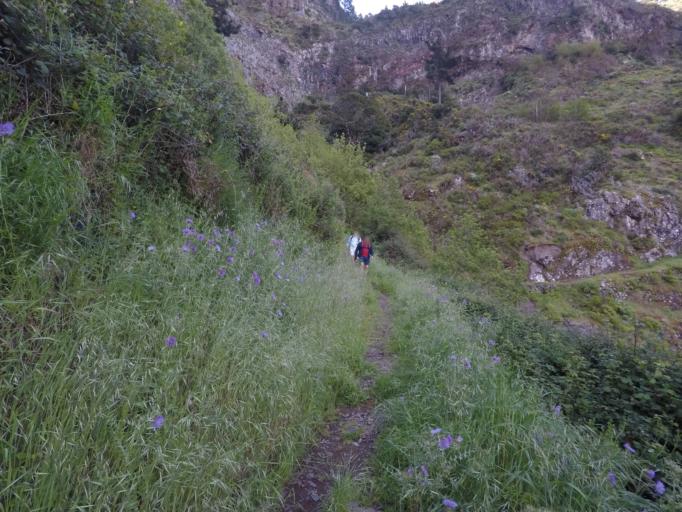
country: PT
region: Madeira
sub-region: Camara de Lobos
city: Curral das Freiras
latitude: 32.7129
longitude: -16.9630
